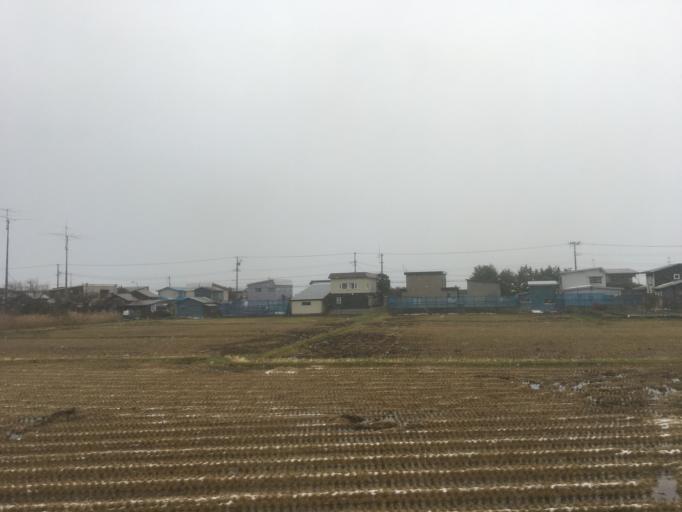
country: JP
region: Aomori
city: Aomori Shi
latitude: 40.9116
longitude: 140.6697
